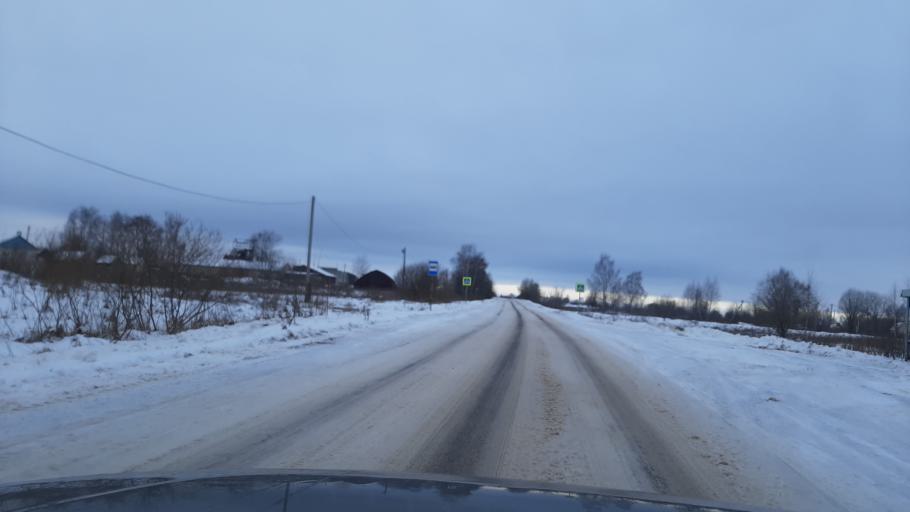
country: RU
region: Kostroma
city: Volgorechensk
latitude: 57.4345
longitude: 41.0672
